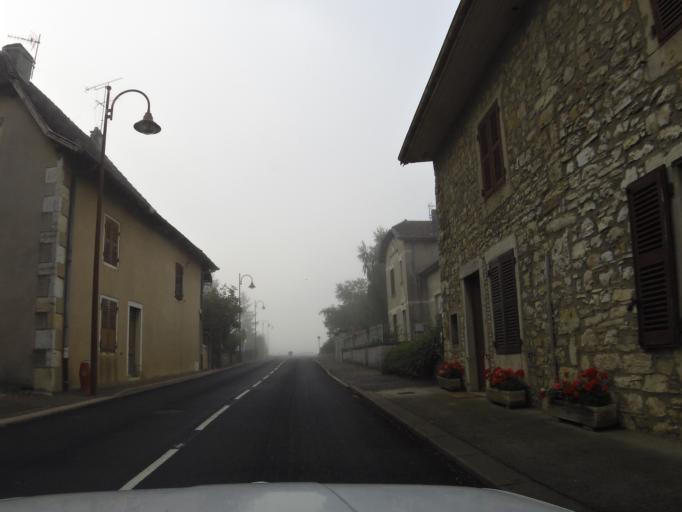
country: FR
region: Rhone-Alpes
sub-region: Departement de l'Isere
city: Creys-Mepieu
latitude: 45.7641
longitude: 5.4812
